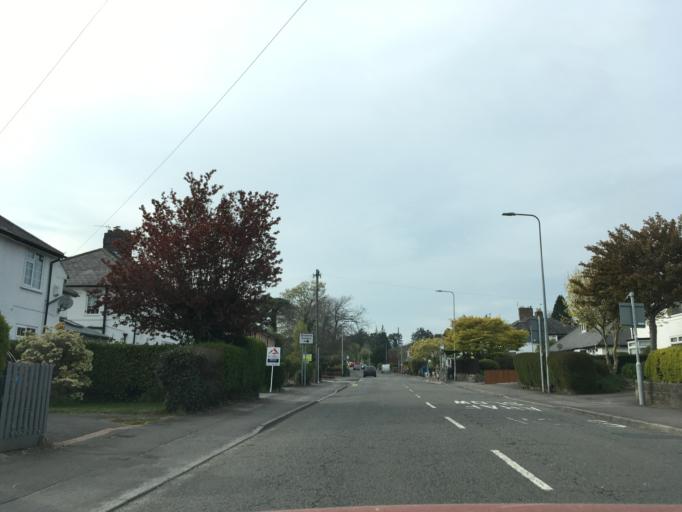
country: GB
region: Wales
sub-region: Cardiff
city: Radyr
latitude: 51.5252
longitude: -3.2150
